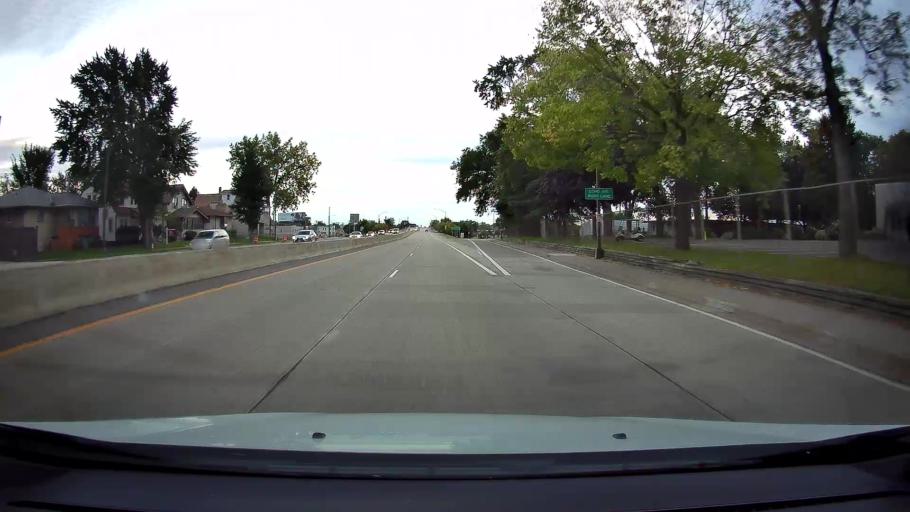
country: US
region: Minnesota
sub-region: Ramsey County
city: Falcon Heights
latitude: 44.9802
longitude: -93.1672
